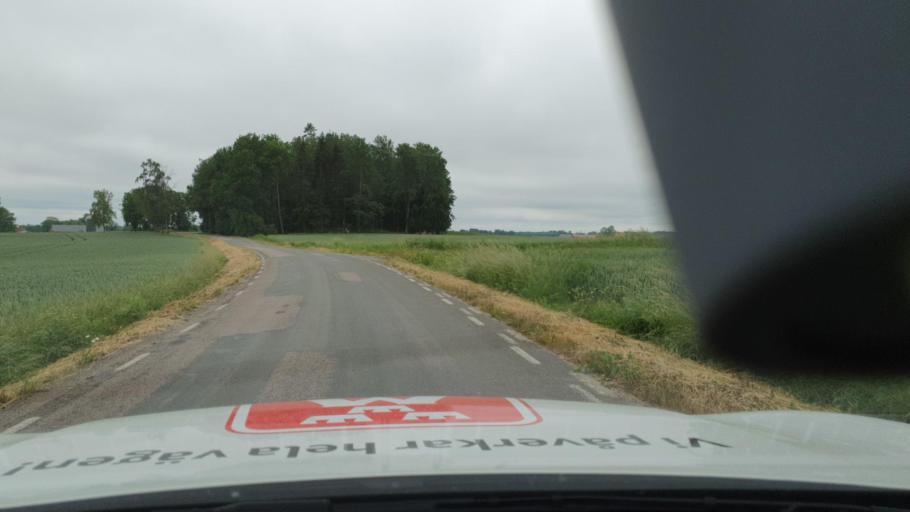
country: SE
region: Vaestra Goetaland
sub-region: Tibro Kommun
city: Tibro
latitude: 58.3626
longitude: 14.0798
